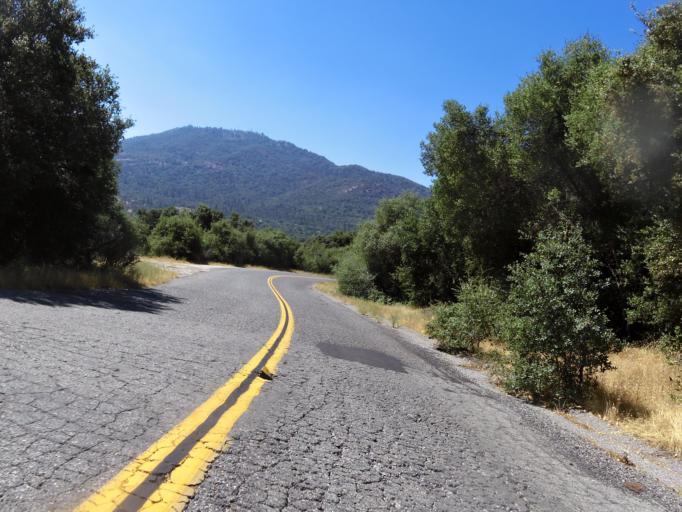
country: US
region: California
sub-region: Madera County
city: Ahwahnee
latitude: 37.3435
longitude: -119.6945
